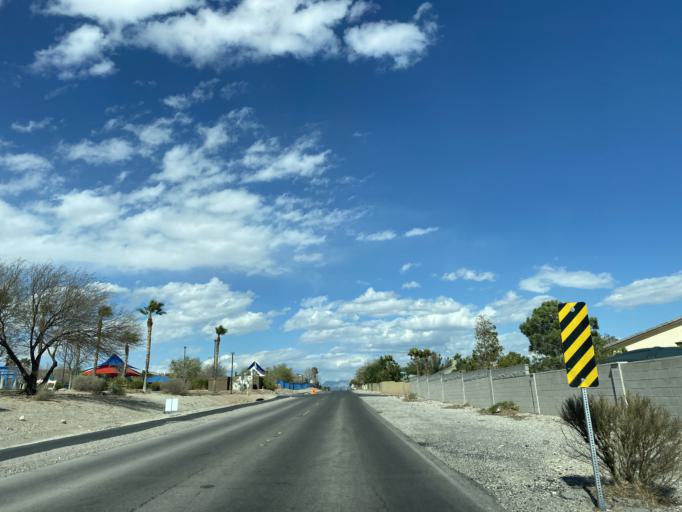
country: US
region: Nevada
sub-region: Clark County
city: Summerlin South
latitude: 36.2417
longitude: -115.3085
